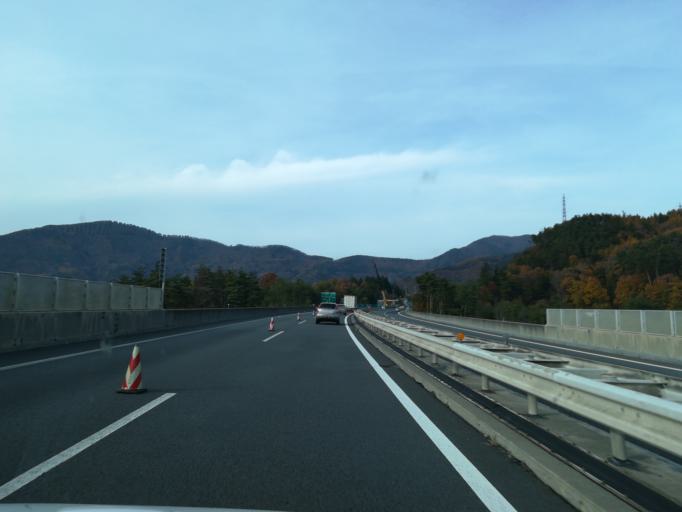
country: JP
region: Nagano
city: Ueda
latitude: 36.4613
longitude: 138.1983
